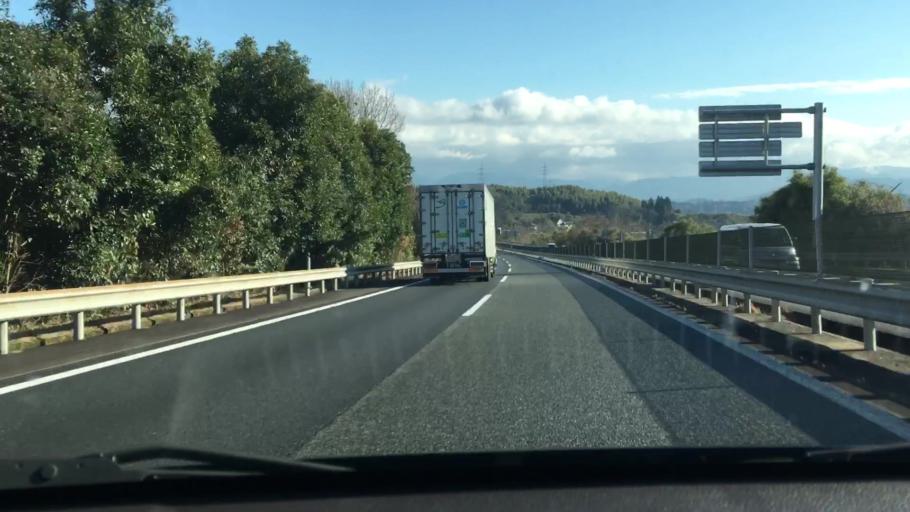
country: JP
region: Kumamoto
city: Hitoyoshi
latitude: 32.2384
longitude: 130.7616
